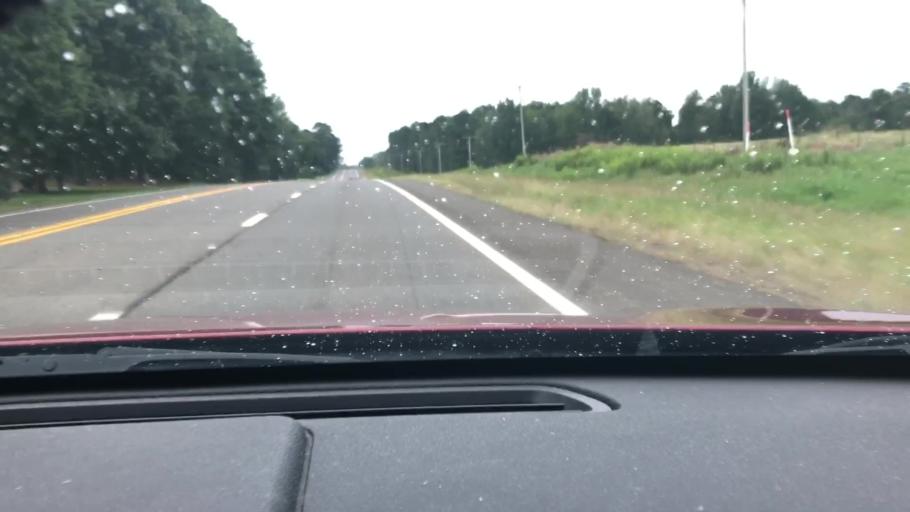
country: US
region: Arkansas
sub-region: Columbia County
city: Waldo
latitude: 33.3512
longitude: -93.3824
